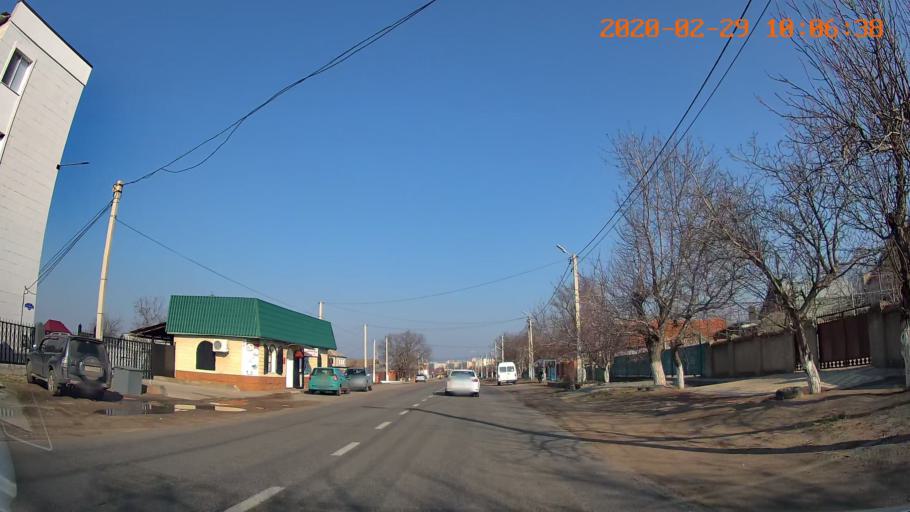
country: MD
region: Telenesti
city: Tiraspolul Nou
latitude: 46.8161
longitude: 29.6689
